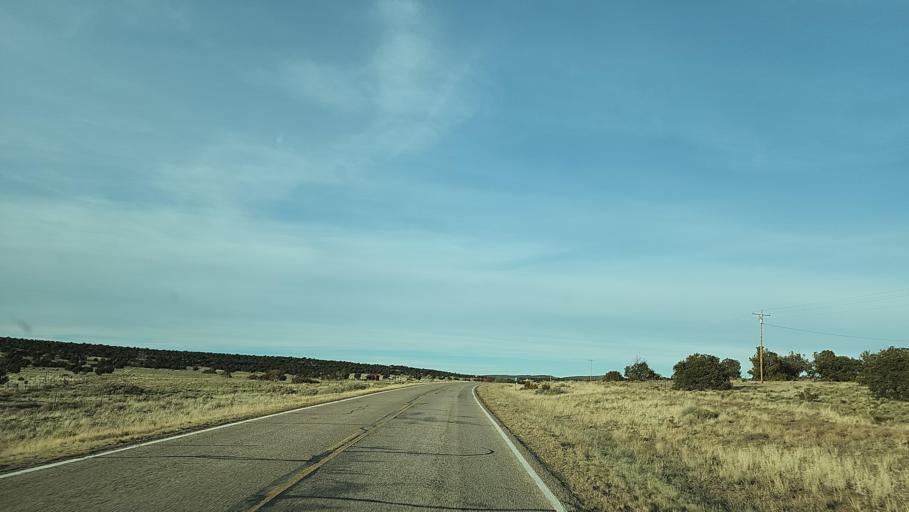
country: US
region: New Mexico
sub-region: Catron County
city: Reserve
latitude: 34.3967
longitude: -108.4447
